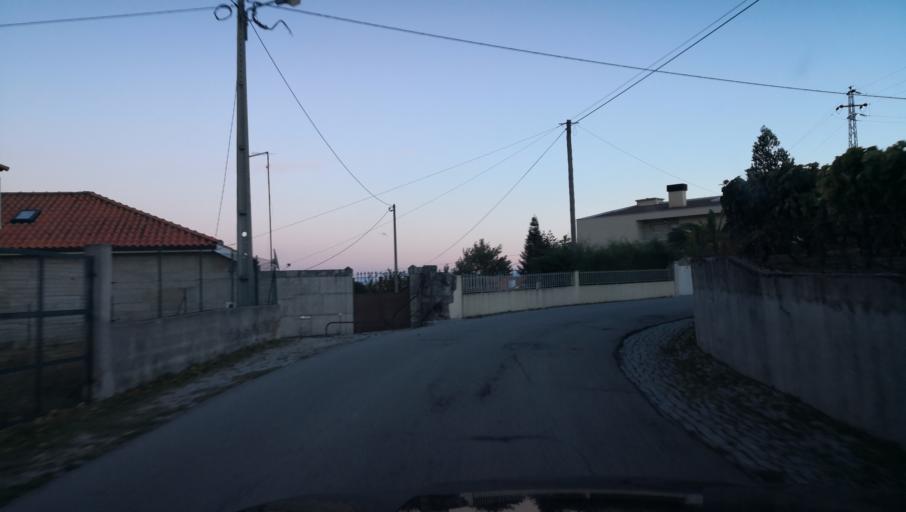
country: PT
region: Vila Real
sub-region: Santa Marta de Penaguiao
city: Santa Marta de Penaguiao
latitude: 41.2627
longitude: -7.7898
